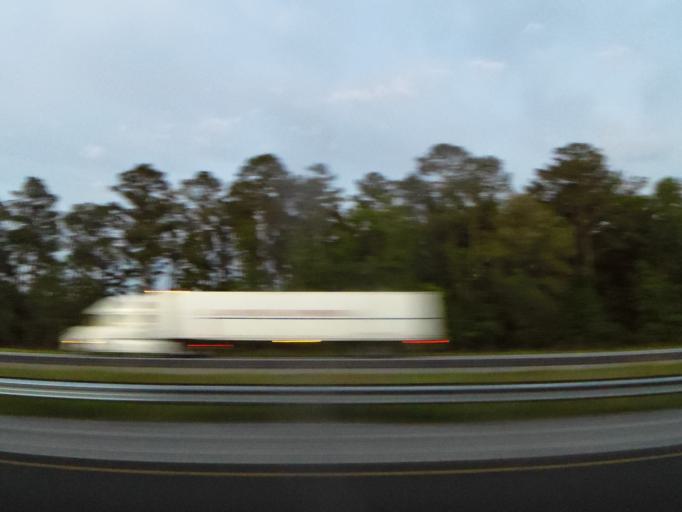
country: US
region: Georgia
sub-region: Liberty County
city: Midway
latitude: 31.7410
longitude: -81.3863
